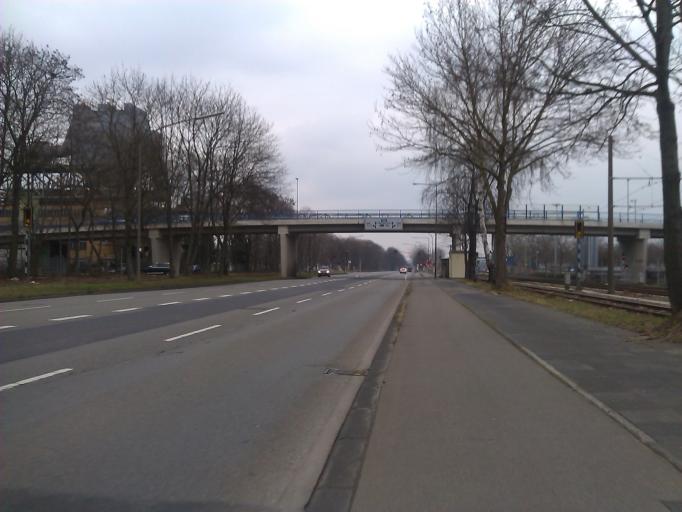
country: DE
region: North Rhine-Westphalia
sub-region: Regierungsbezirk Koln
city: Leverkusen
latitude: 51.0092
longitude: 6.9552
